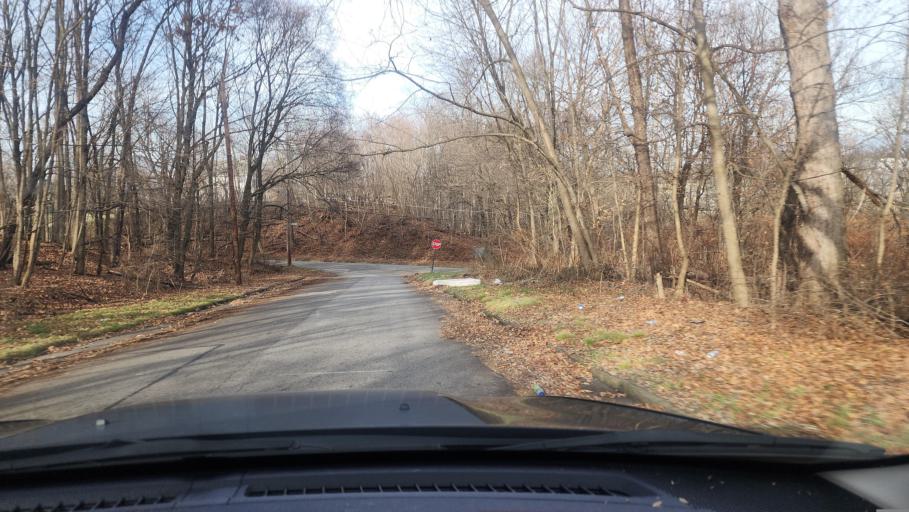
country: US
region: Ohio
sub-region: Mahoning County
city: Youngstown
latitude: 41.1018
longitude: -80.6249
